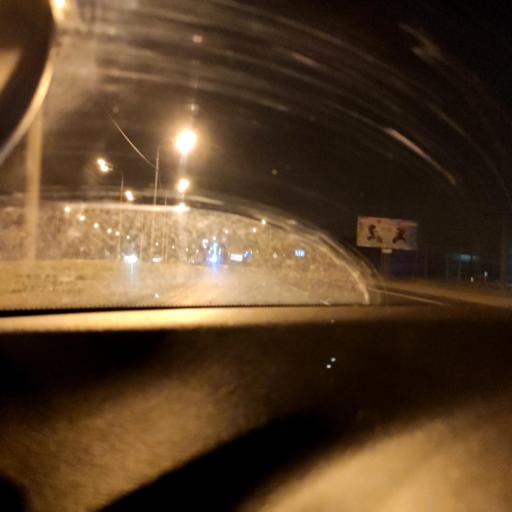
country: RU
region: Samara
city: Smyshlyayevka
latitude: 53.2589
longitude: 50.3760
